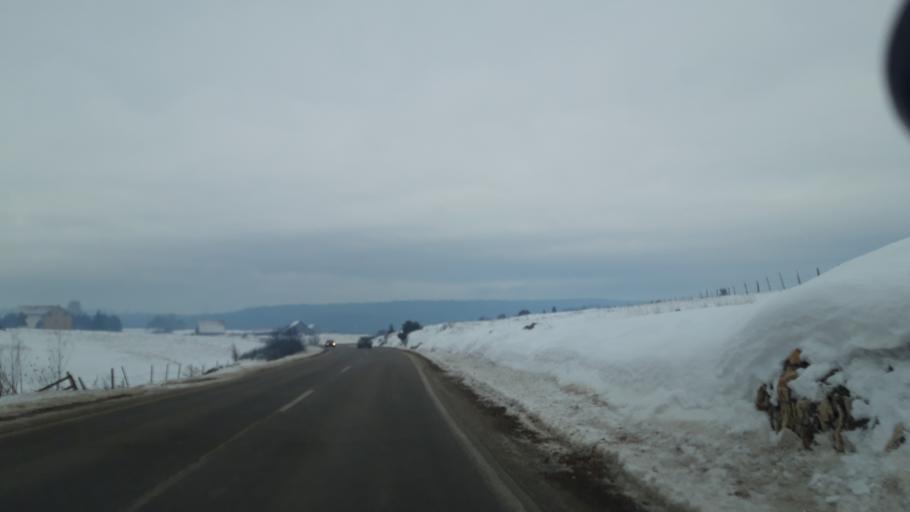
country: BA
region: Republika Srpska
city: Sokolac
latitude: 43.9379
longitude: 18.8243
